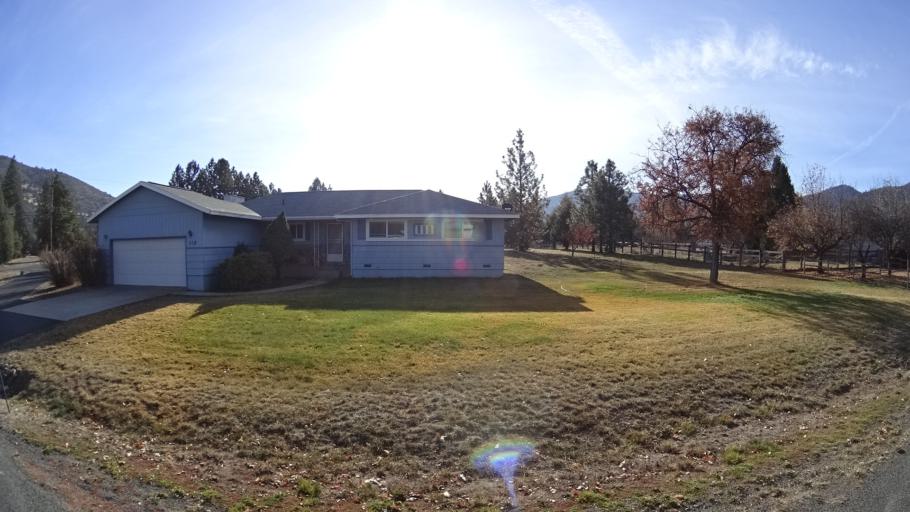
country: US
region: California
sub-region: Siskiyou County
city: Yreka
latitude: 41.6831
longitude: -122.6366
